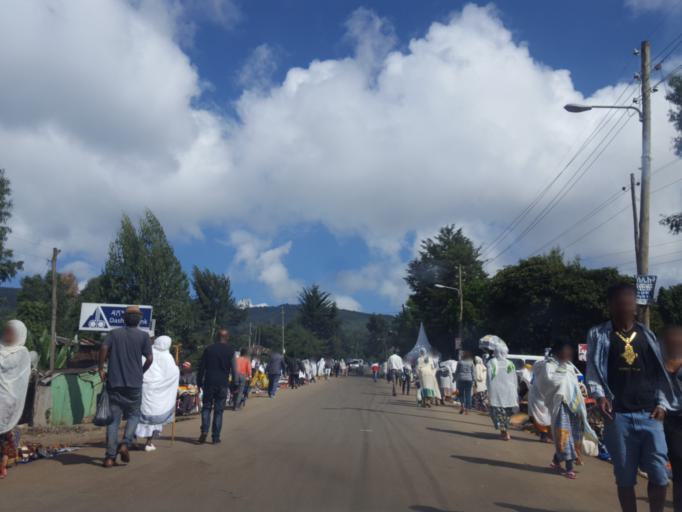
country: ET
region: Adis Abeba
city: Addis Ababa
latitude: 9.0690
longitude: 38.7608
